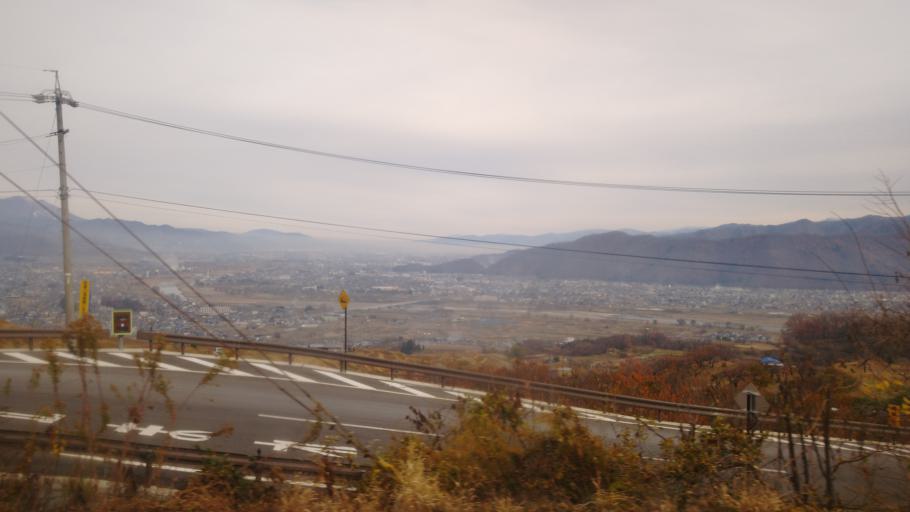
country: JP
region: Nagano
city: Nagano-shi
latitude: 36.4998
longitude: 138.0976
